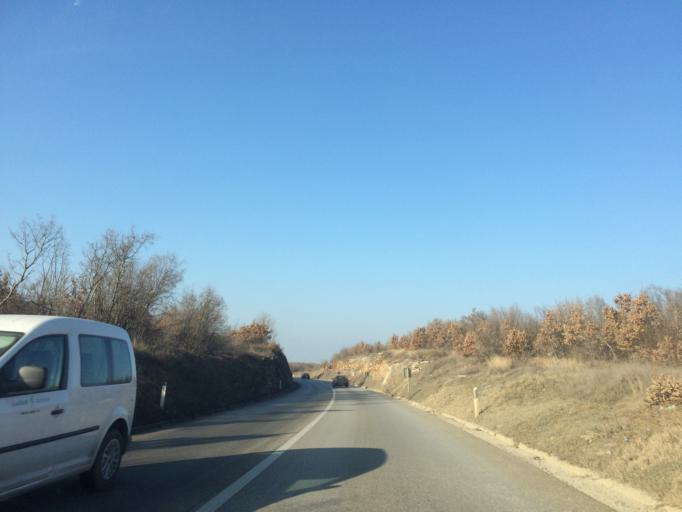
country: XK
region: Pec
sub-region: Komuna e Klines
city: Klina
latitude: 42.5974
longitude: 20.6251
